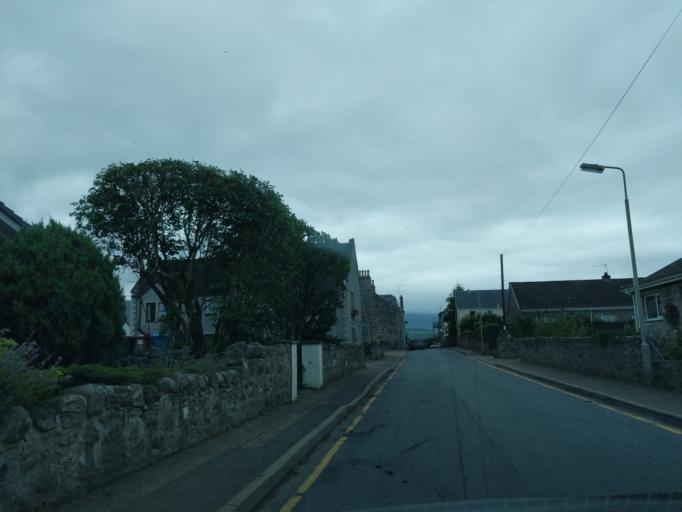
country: GB
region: Scotland
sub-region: Highland
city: Grantown on Spey
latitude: 57.3316
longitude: -3.6102
